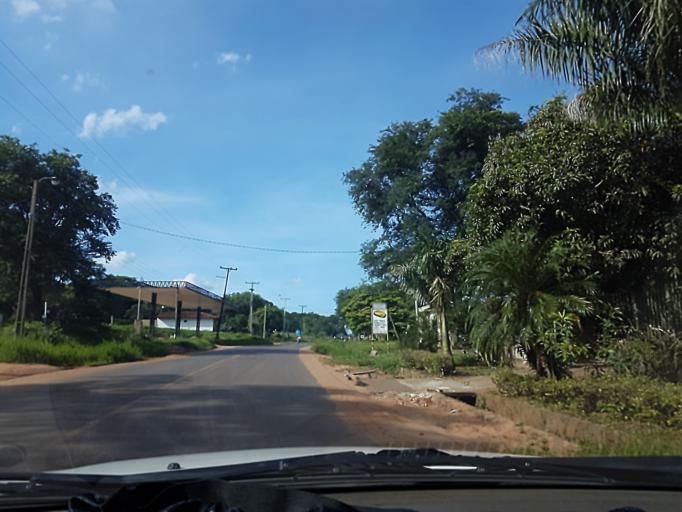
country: PY
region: Central
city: Limpio
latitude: -25.2249
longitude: -57.4491
